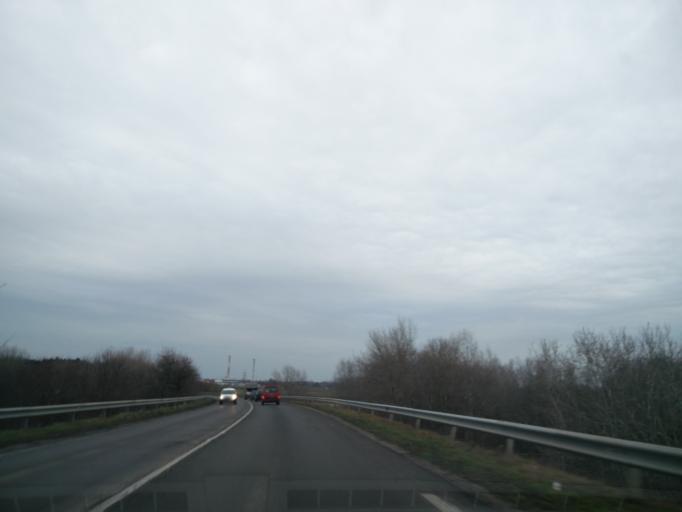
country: HU
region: Pest
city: Vecses
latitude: 47.3931
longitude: 19.3096
